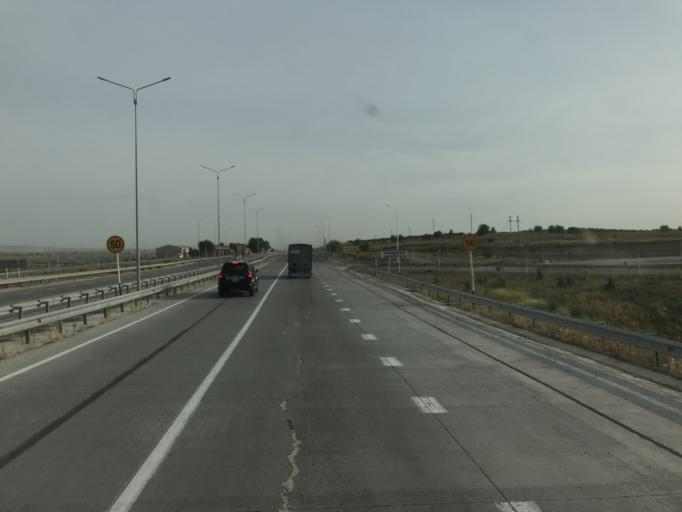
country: KZ
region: Ongtustik Qazaqstan
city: Qazyqurt
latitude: 41.6866
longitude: 69.3942
